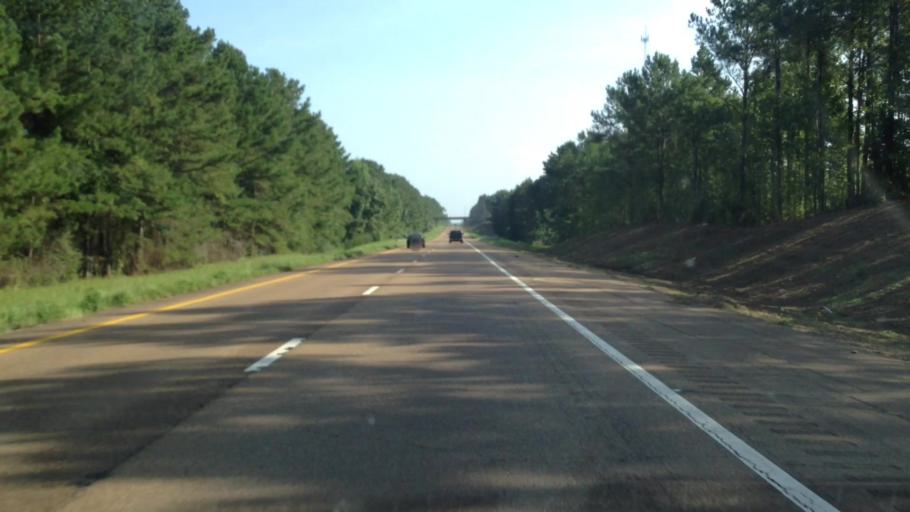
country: US
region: Mississippi
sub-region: Lincoln County
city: Brookhaven
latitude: 31.4706
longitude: -90.4786
